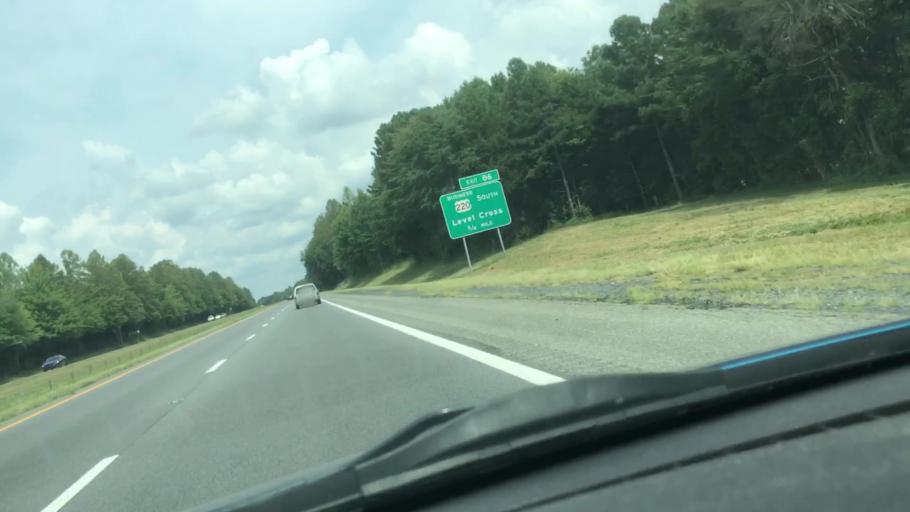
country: US
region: North Carolina
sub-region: Randolph County
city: Randleman
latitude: 35.8660
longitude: -79.8181
